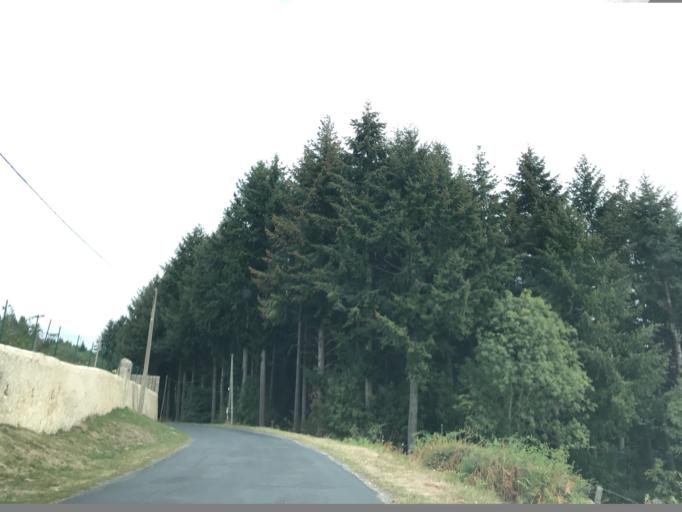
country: FR
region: Auvergne
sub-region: Departement du Puy-de-Dome
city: Celles-sur-Durolle
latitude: 45.8218
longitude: 3.6134
